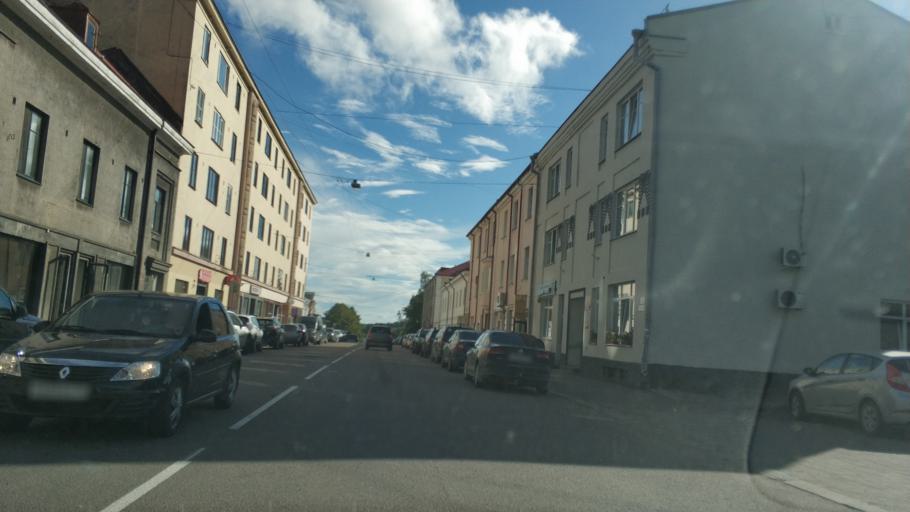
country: RU
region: Republic of Karelia
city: Sortavala
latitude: 61.7022
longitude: 30.6916
